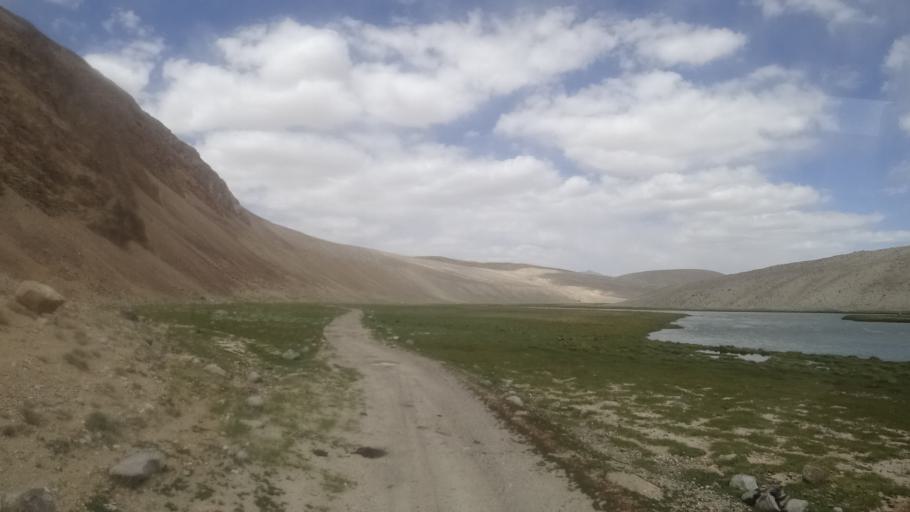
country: AF
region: Badakhshan
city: Khandud
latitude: 37.3966
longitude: 73.1429
